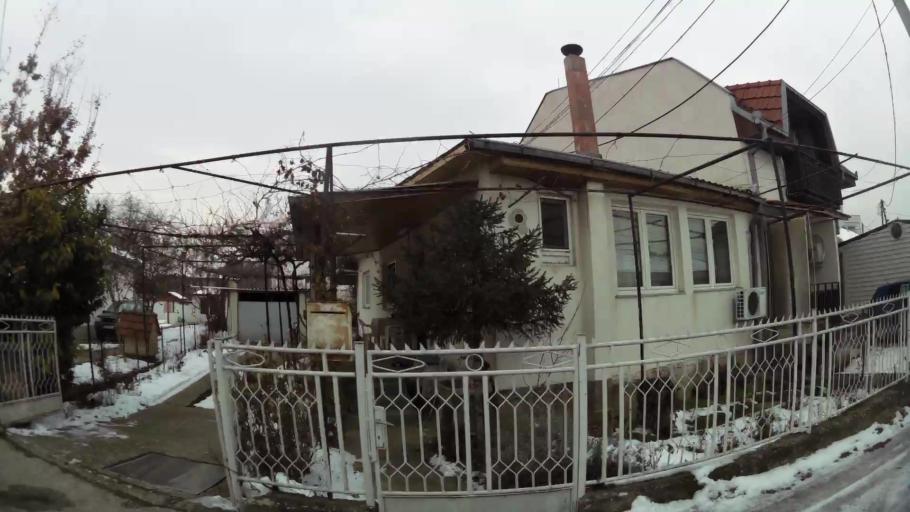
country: MK
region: Butel
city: Butel
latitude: 42.0377
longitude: 21.4509
